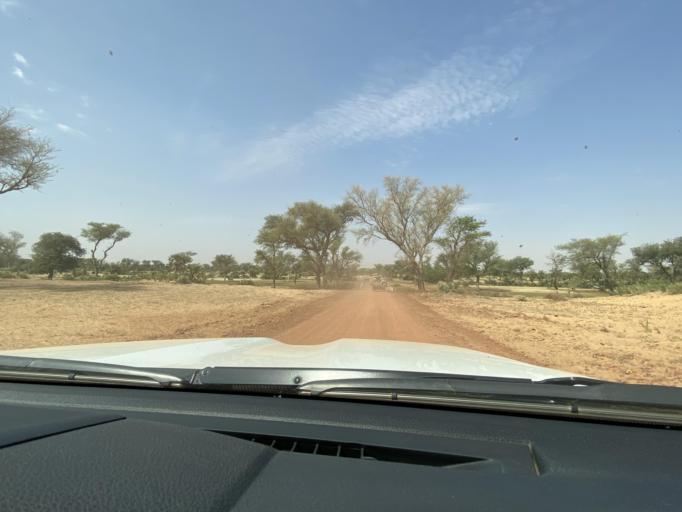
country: NE
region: Dosso
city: Birnin Gaoure
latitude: 13.2462
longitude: 2.8587
